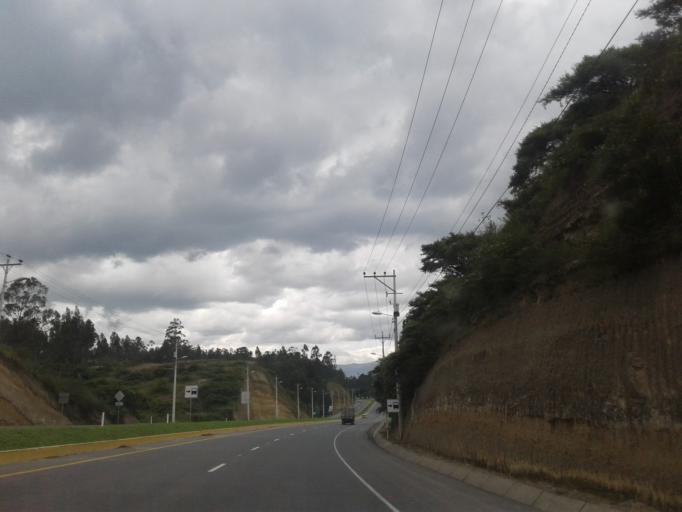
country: EC
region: Pichincha
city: Sangolqui
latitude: -0.3151
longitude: -78.3671
